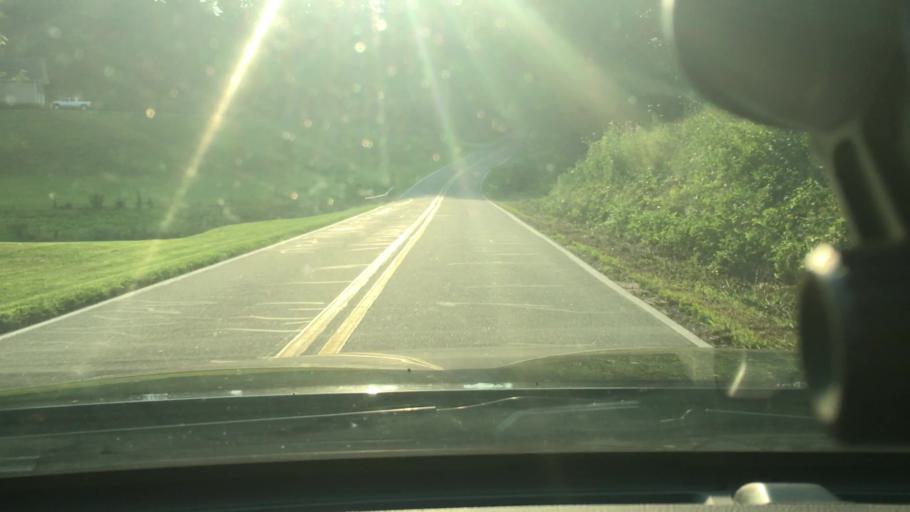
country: US
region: North Carolina
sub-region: McDowell County
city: West Marion
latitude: 35.6278
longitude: -81.9918
